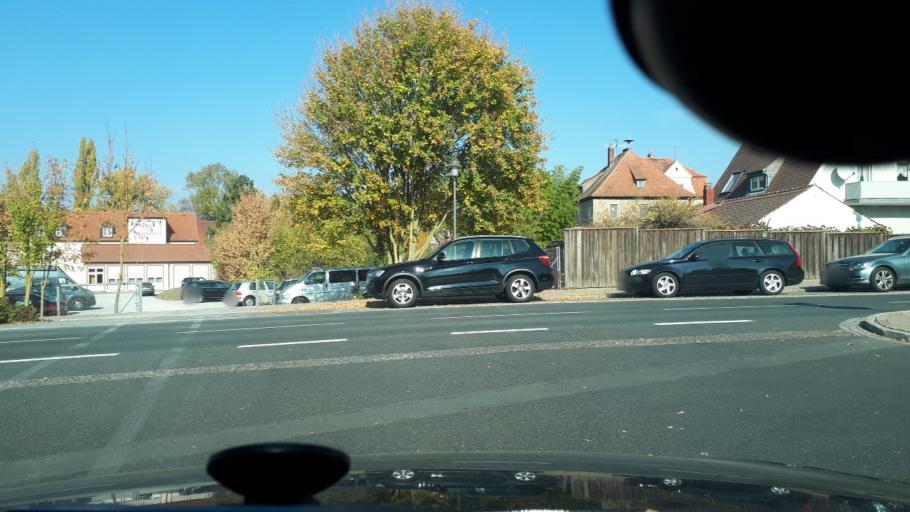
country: DE
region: Bavaria
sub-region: Regierungsbezirk Unterfranken
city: Sommerach
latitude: 49.8041
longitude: 10.2290
